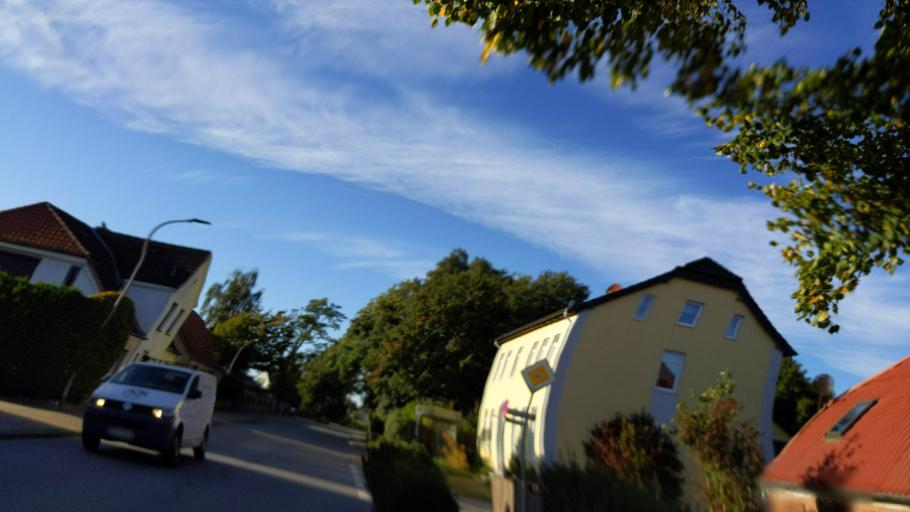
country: DE
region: Schleswig-Holstein
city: Ahrensbok
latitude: 54.0180
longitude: 10.5717
